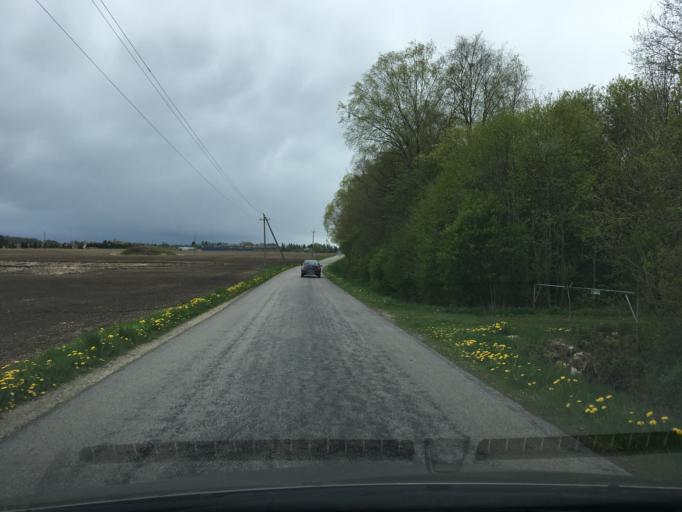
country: EE
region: Harju
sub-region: Joelaehtme vald
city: Loo
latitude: 59.3752
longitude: 24.9661
